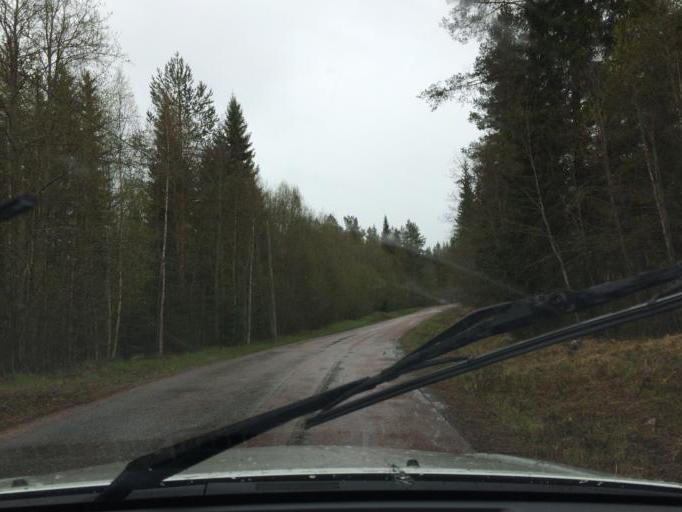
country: SE
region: Dalarna
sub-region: Ludvika Kommun
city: Abborrberget
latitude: 60.0453
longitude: 14.7401
